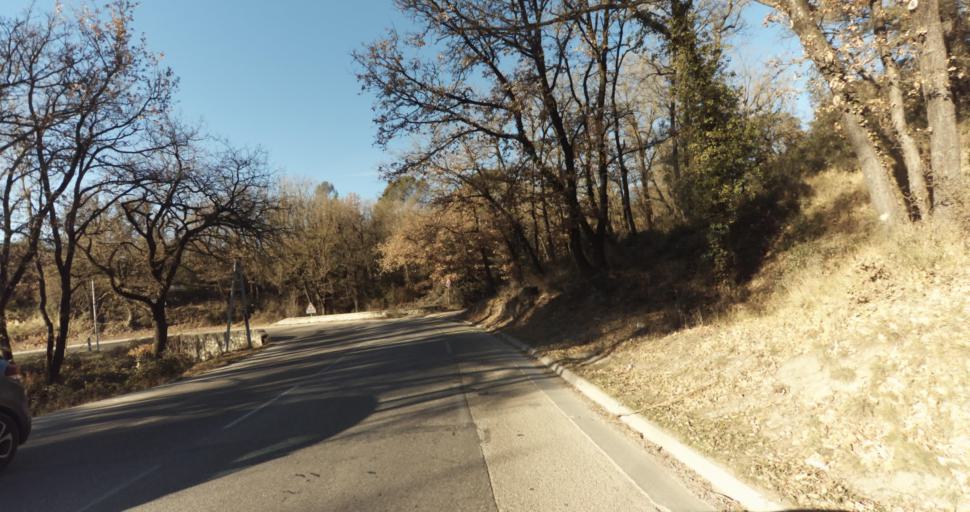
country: FR
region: Provence-Alpes-Cote d'Azur
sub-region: Departement des Bouches-du-Rhone
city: Cadolive
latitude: 43.4017
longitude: 5.5647
